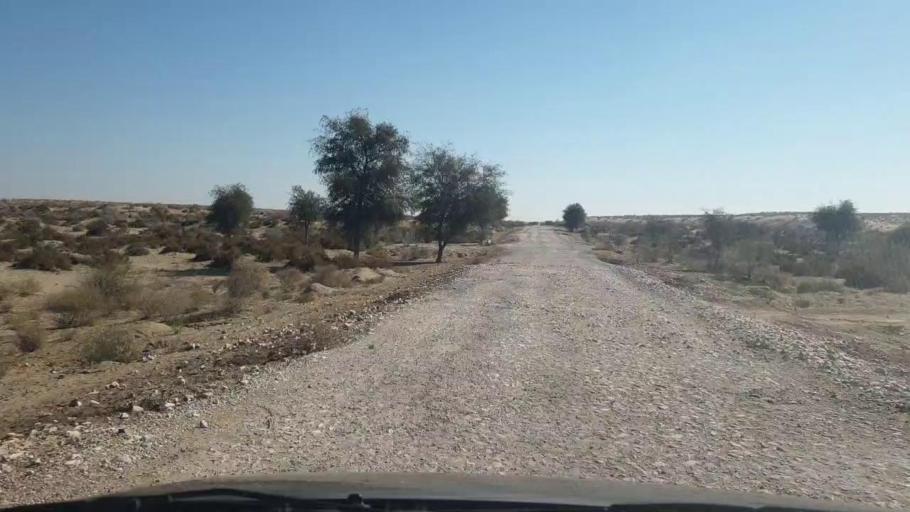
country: PK
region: Sindh
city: Bozdar
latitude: 27.0419
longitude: 68.6876
